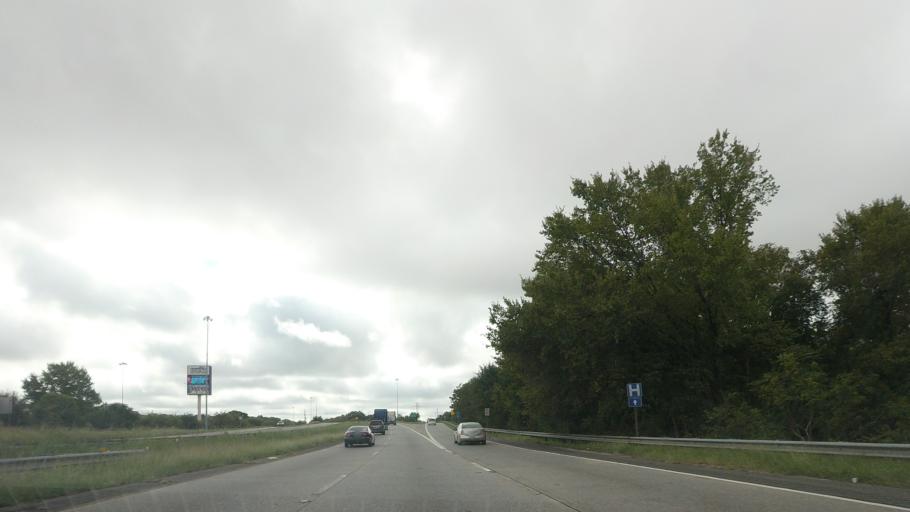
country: US
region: Georgia
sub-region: Bibb County
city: Macon
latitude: 32.8418
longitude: -83.6224
